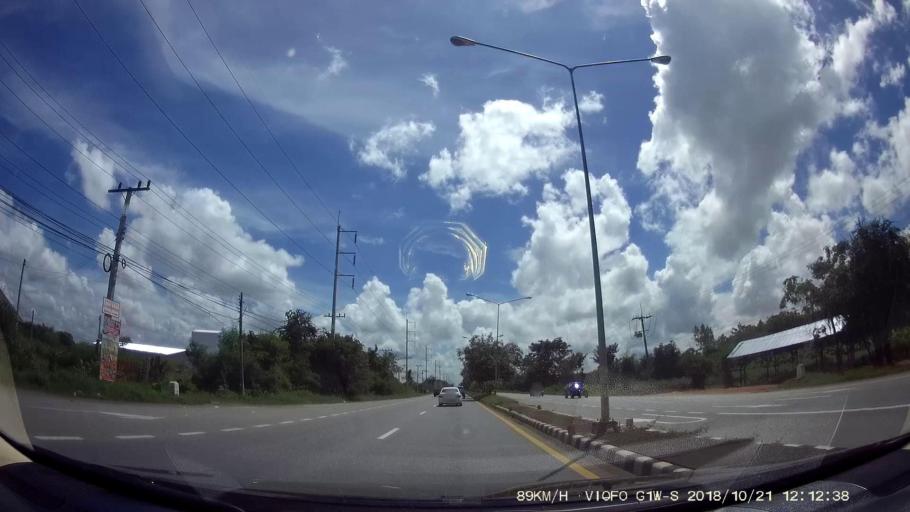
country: TH
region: Chaiyaphum
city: Chatturat
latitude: 15.4044
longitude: 101.8359
